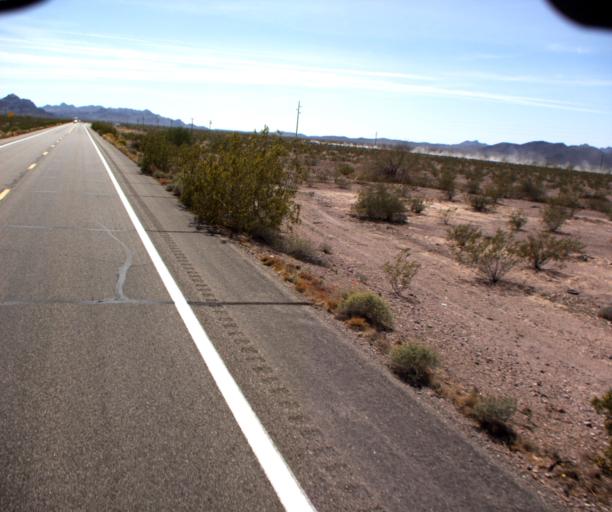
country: US
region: Arizona
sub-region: La Paz County
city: Quartzsite
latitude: 33.3450
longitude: -114.2171
